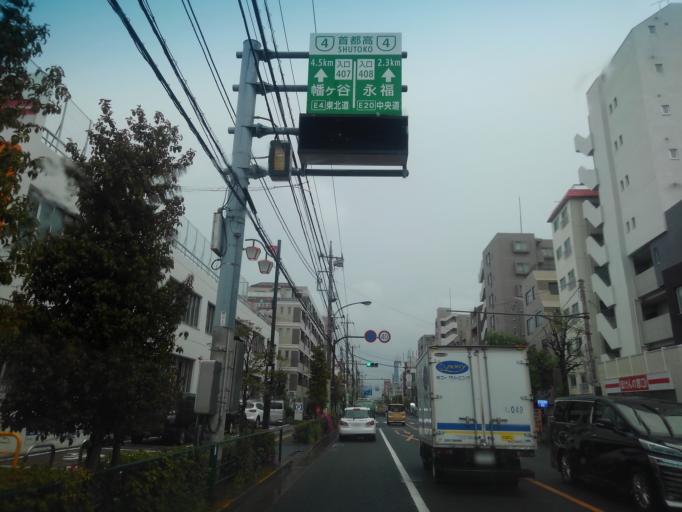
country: JP
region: Tokyo
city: Tokyo
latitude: 35.6813
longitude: 139.6337
